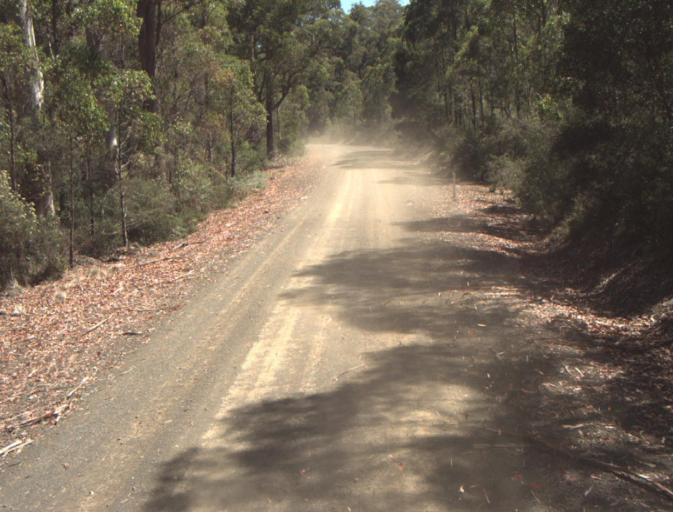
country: AU
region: Tasmania
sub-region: Launceston
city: Newstead
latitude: -41.3058
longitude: 147.3344
